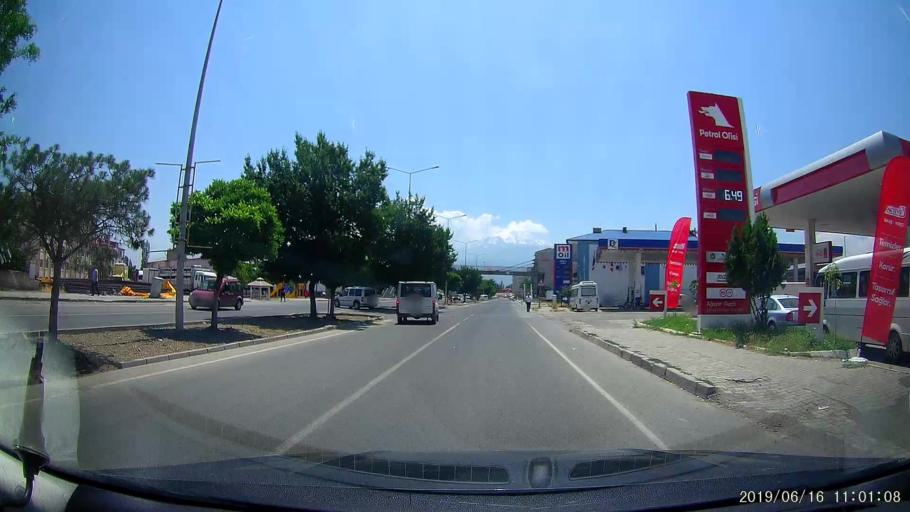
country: TR
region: Igdir
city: Igdir
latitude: 39.9168
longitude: 44.0475
